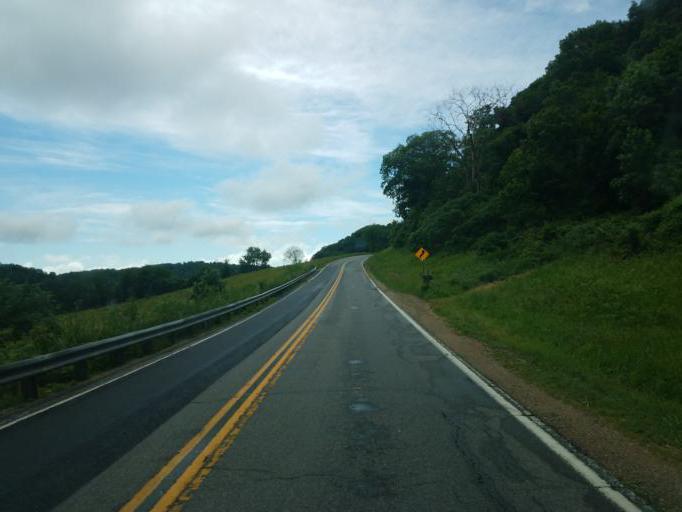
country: US
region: Wisconsin
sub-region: Vernon County
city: Hillsboro
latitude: 43.6605
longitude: -90.4146
